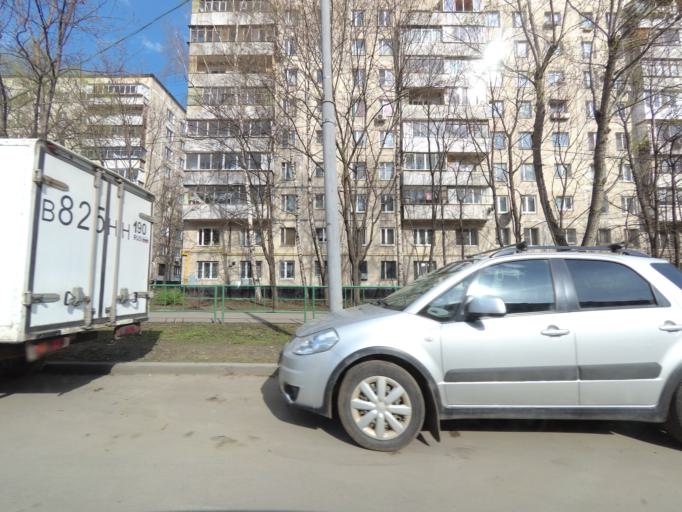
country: RU
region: Moscow
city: Gol'yanovo
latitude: 55.8218
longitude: 37.8259
